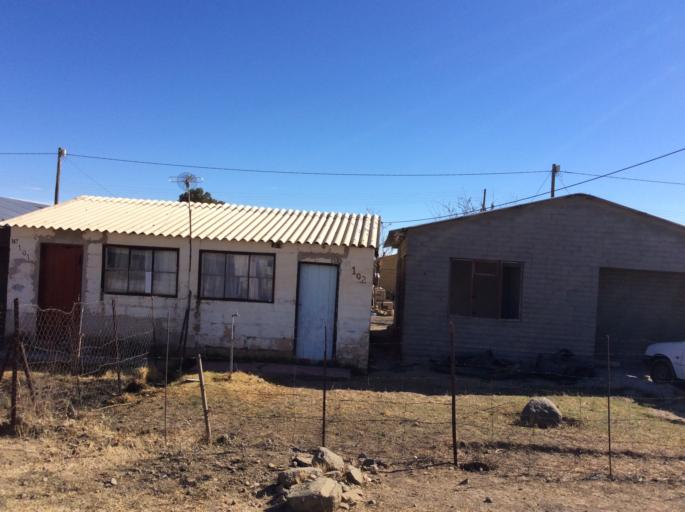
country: ZA
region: Orange Free State
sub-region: Lejweleputswa District Municipality
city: Brandfort
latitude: -28.7360
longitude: 26.1089
